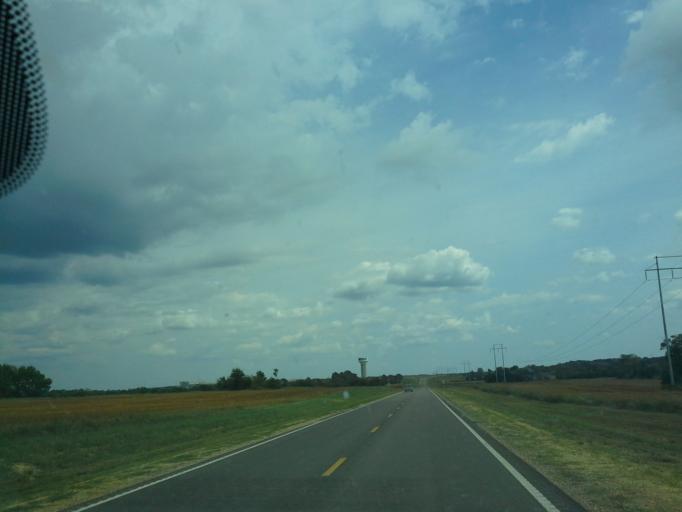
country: US
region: Mississippi
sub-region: Clay County
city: West Point
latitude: 33.6368
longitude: -88.6266
